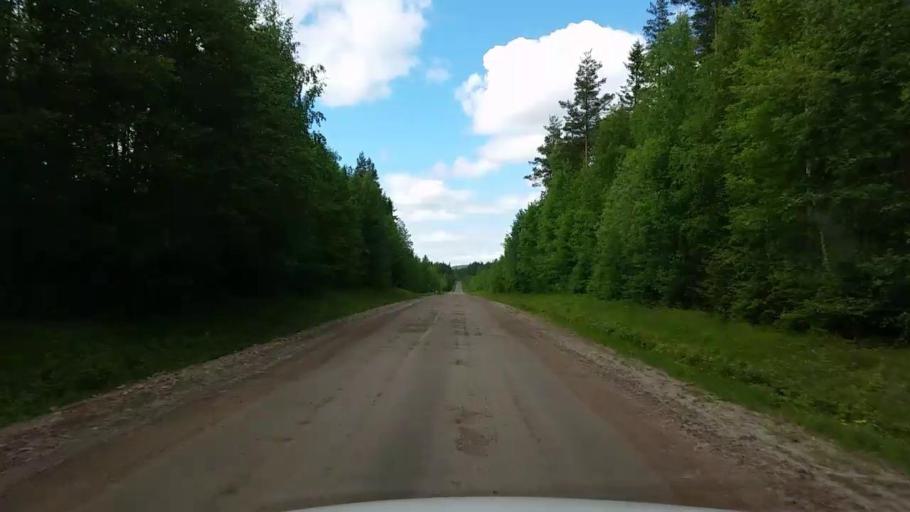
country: SE
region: Gaevleborg
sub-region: Ovanakers Kommun
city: Alfta
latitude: 61.4850
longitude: 15.9901
